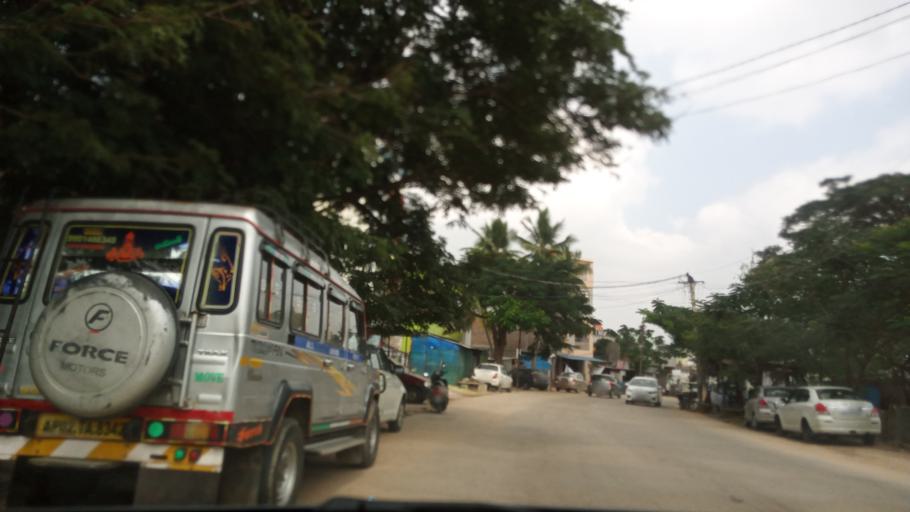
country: IN
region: Andhra Pradesh
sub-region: Chittoor
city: Madanapalle
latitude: 13.6354
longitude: 78.6284
